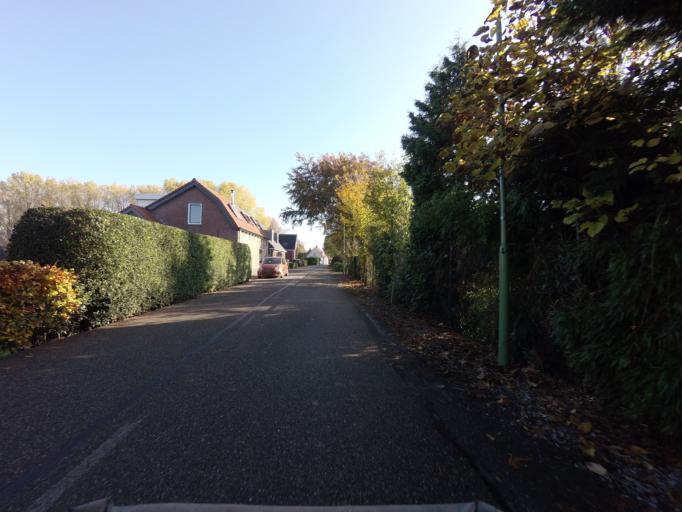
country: NL
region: North Brabant
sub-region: Gemeente Woudrichem
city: Almkerk
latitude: 51.7323
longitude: 4.9550
